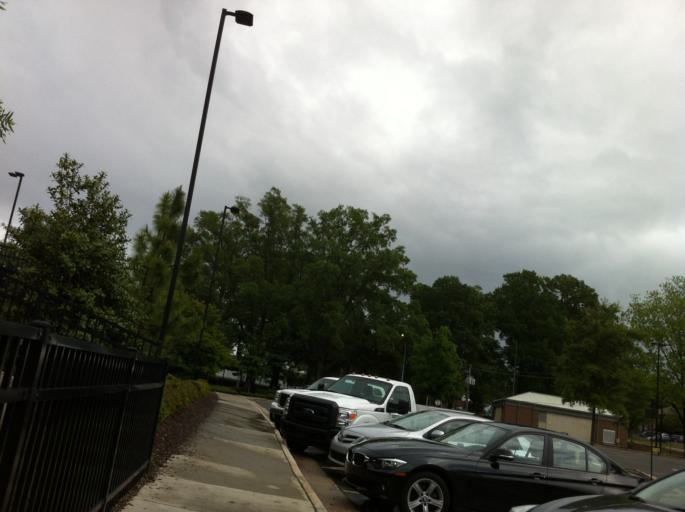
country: US
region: North Carolina
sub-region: Wake County
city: West Raleigh
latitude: 35.7796
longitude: -78.6626
